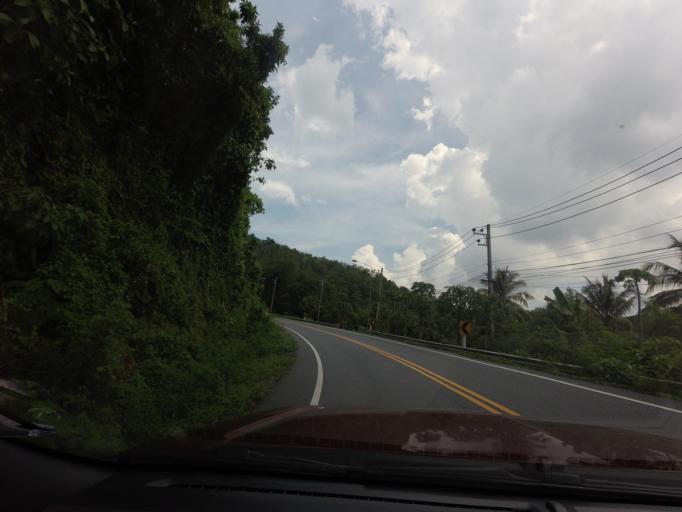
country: TH
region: Yala
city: Than To
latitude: 6.0403
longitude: 101.2083
